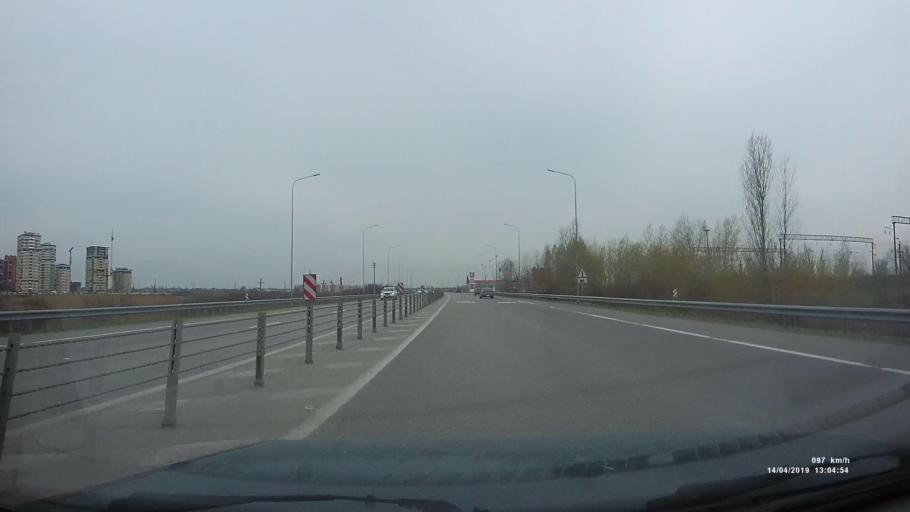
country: RU
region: Rostov
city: Bataysk
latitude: 47.1546
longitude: 39.7212
